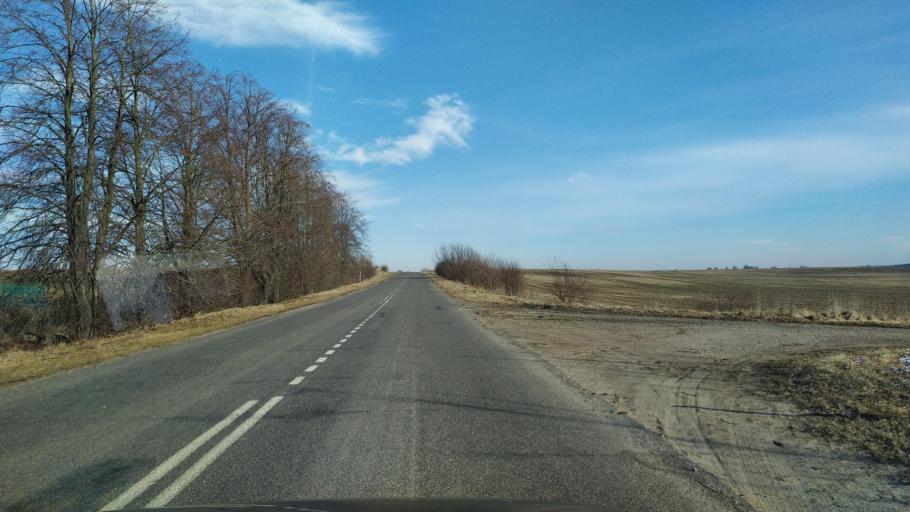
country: BY
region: Brest
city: Kamyanyets
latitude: 52.4129
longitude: 23.8006
